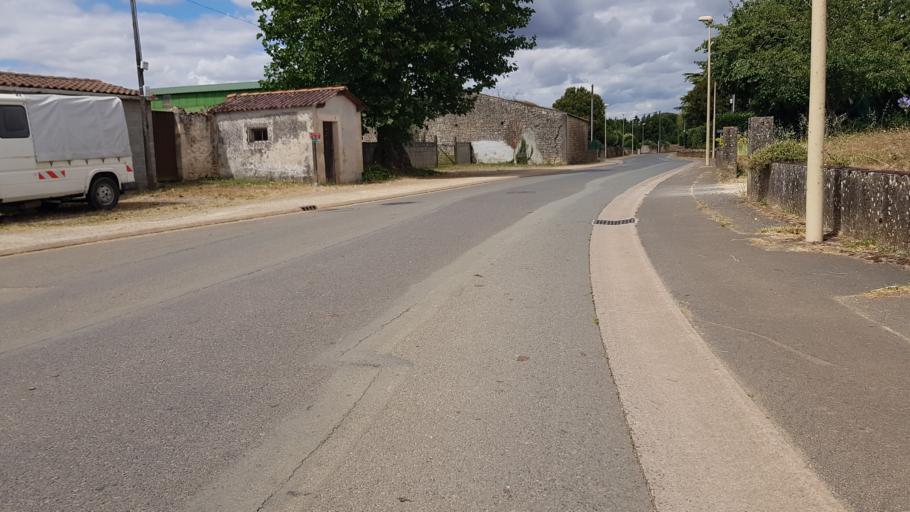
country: FR
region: Poitou-Charentes
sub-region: Departement des Deux-Sevres
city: Vouille
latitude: 46.3058
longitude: -0.3414
